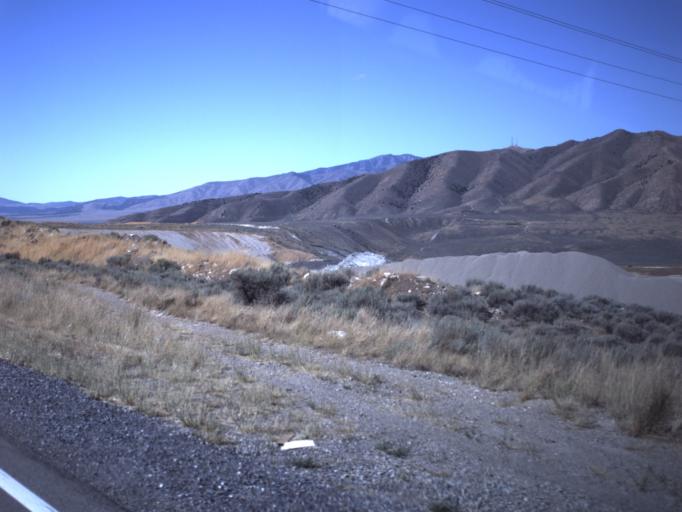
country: US
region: Utah
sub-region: Tooele County
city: Tooele
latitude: 40.4729
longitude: -112.3496
